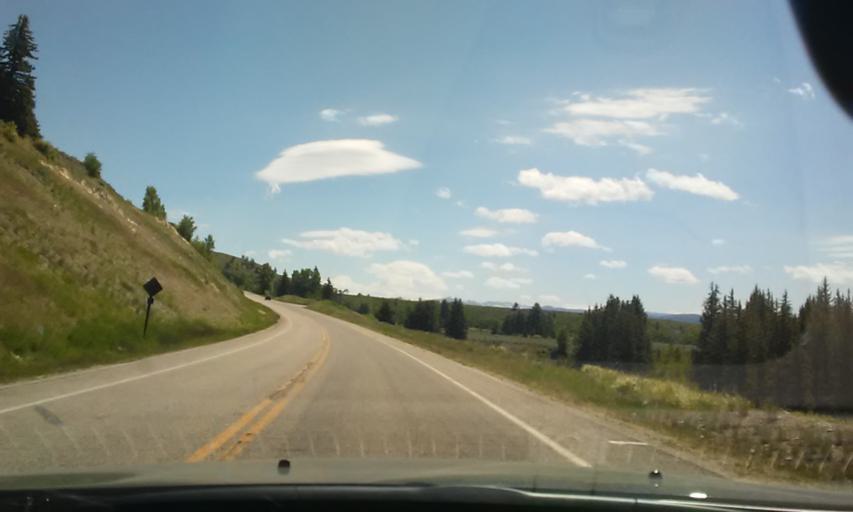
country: US
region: Wyoming
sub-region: Teton County
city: Jackson
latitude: 43.8373
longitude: -110.4997
